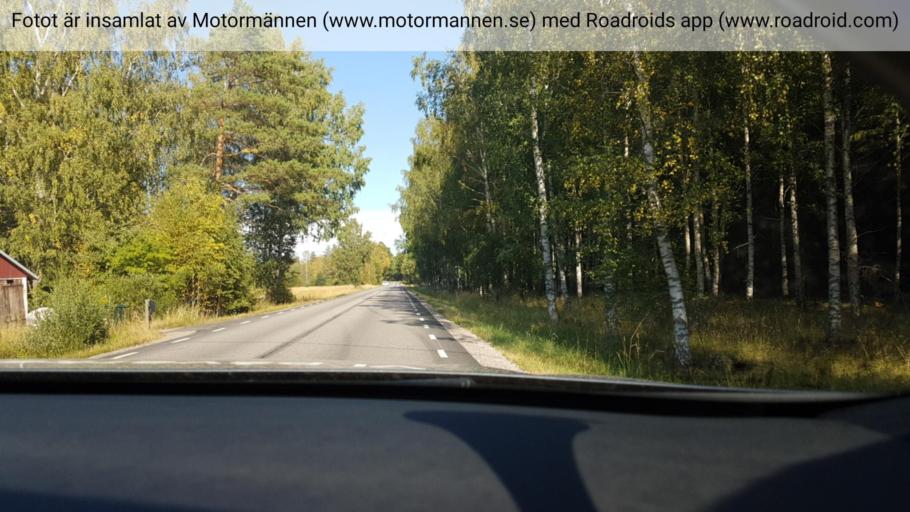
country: SE
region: Vaestra Goetaland
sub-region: Gotene Kommun
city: Goetene
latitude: 58.6308
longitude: 13.5131
